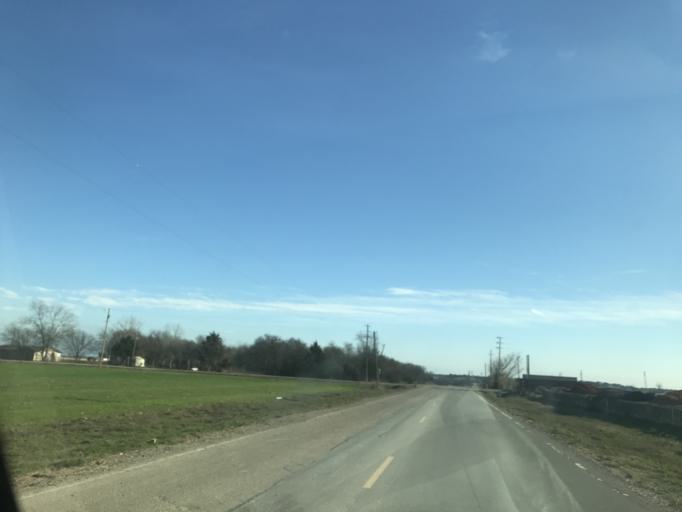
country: US
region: Texas
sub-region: Dallas County
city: Wilmer
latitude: 32.5669
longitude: -96.6698
